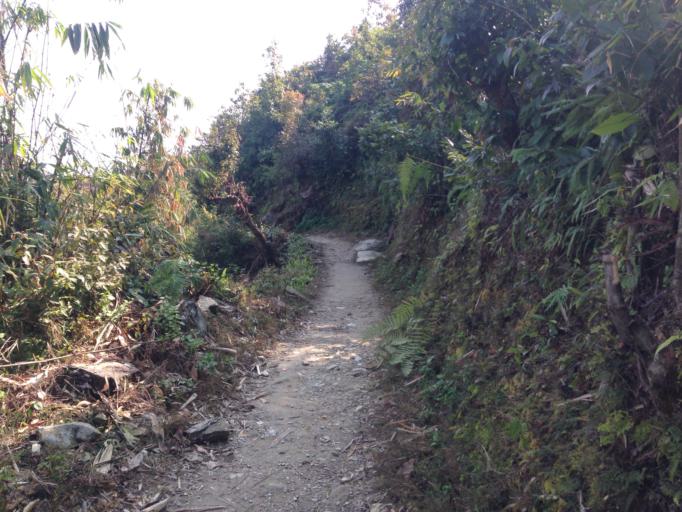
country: NP
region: Western Region
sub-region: Gandaki Zone
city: Pokhara
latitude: 28.2015
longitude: 83.9411
